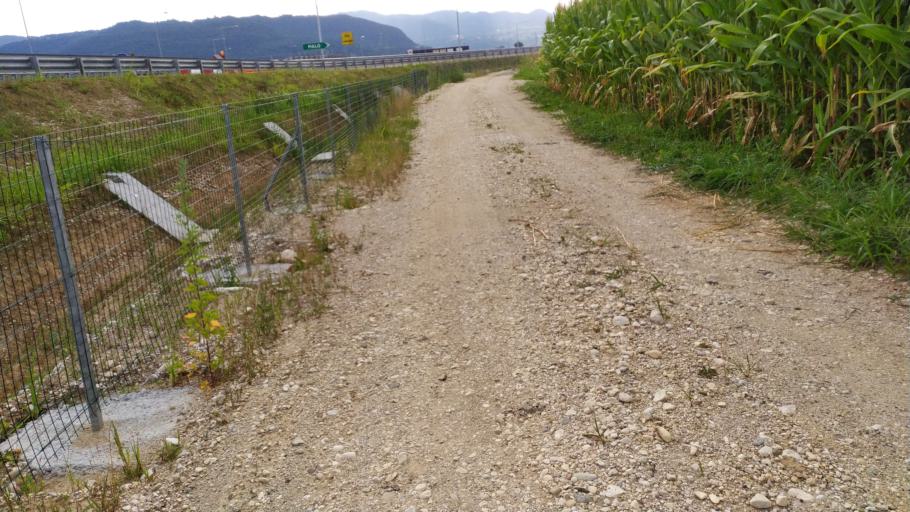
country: IT
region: Veneto
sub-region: Provincia di Vicenza
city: Isola Vicentina
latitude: 45.6491
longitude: 11.4492
